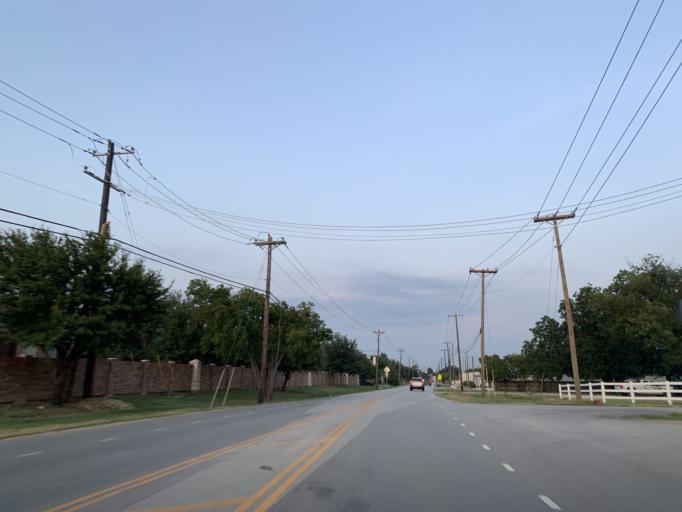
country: US
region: Texas
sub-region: Tarrant County
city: Keller
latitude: 32.9388
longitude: -97.2717
